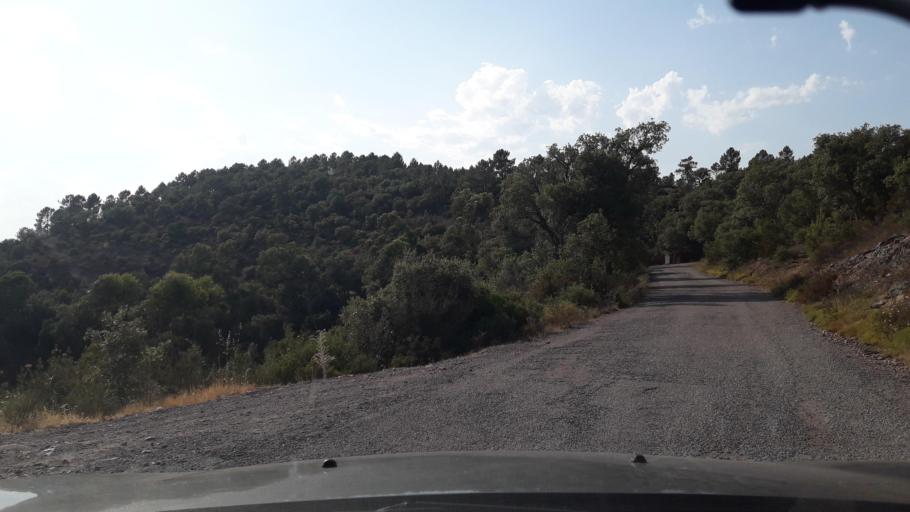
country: FR
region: Provence-Alpes-Cote d'Azur
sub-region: Departement du Var
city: Saint-Raphael
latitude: 43.4968
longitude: 6.8061
